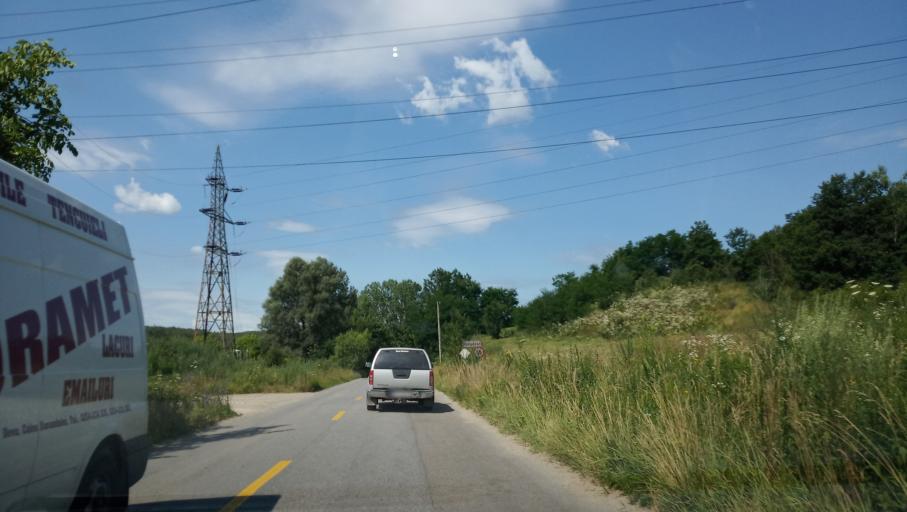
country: RO
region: Hunedoara
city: Hunedoara
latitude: 45.7360
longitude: 22.9156
